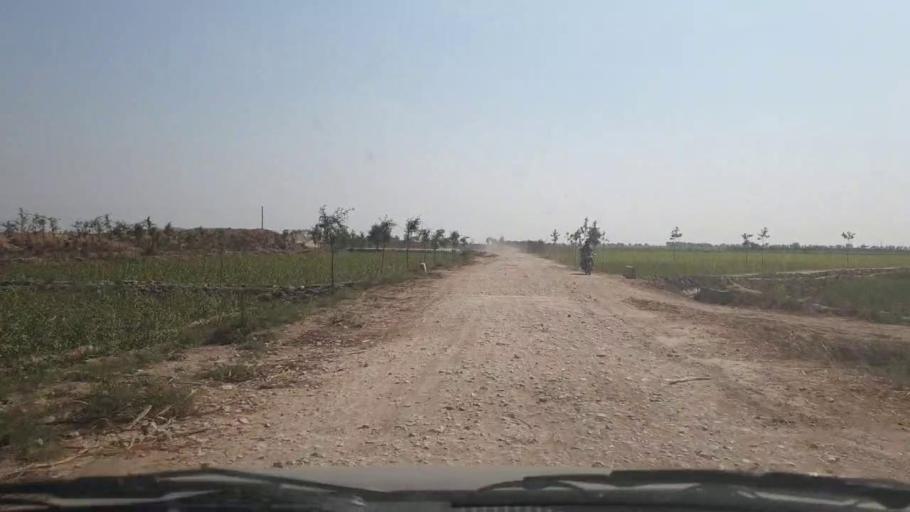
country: PK
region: Sindh
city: Samaro
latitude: 25.2515
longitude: 69.3552
